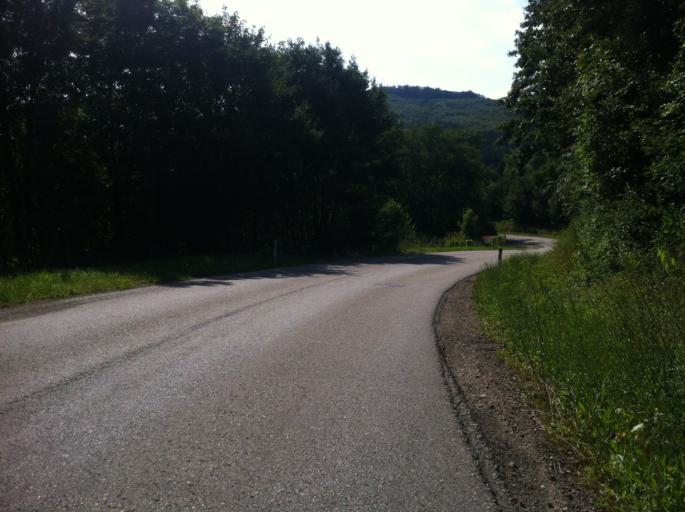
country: AT
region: Lower Austria
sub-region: Politischer Bezirk Wien-Umgebung
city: Wolfsgraben
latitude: 48.1712
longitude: 16.1288
